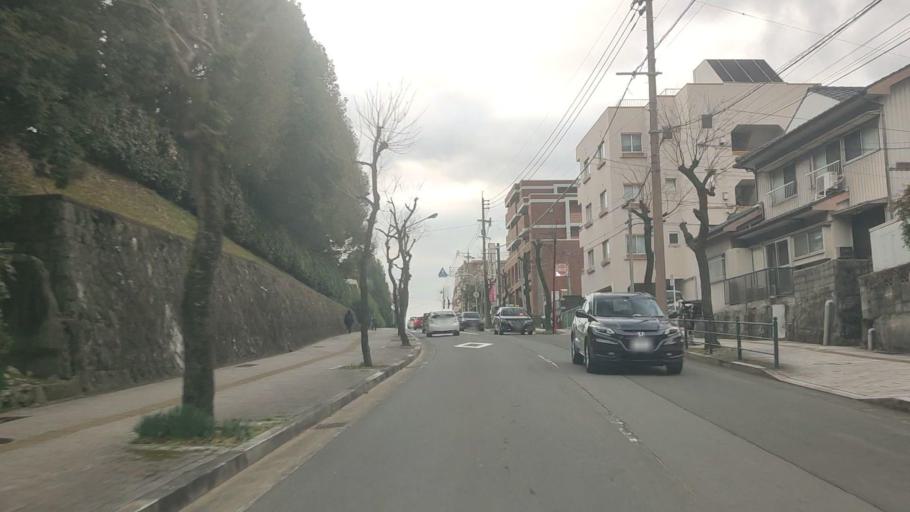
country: JP
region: Nagasaki
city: Nagasaki-shi
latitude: 32.7745
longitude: 129.8674
